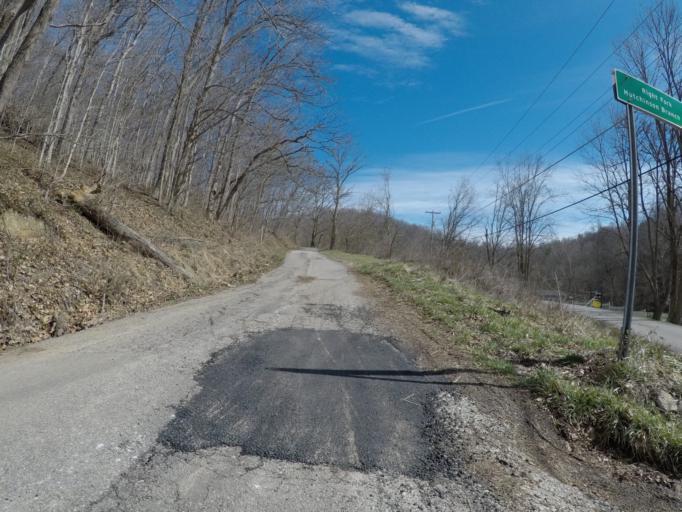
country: US
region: West Virginia
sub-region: Wayne County
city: Ceredo
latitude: 38.3478
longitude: -82.5617
